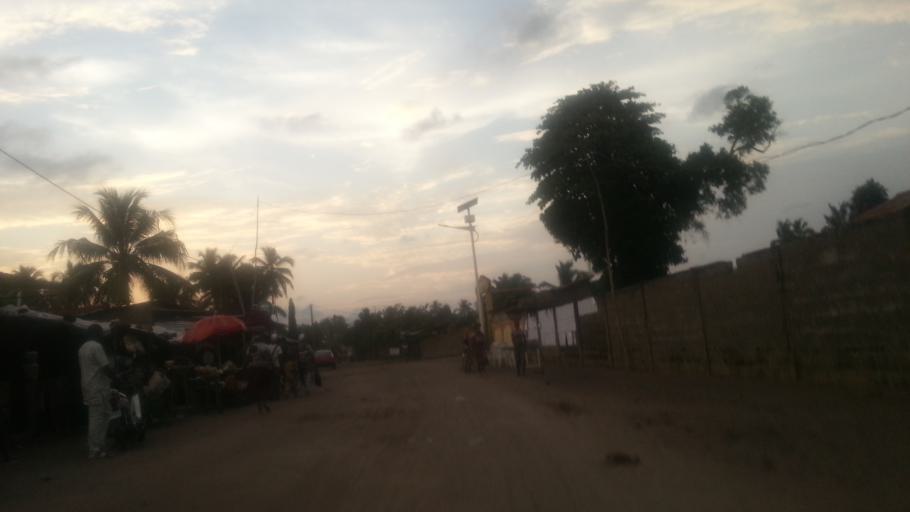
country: BJ
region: Littoral
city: Cotonou
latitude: 6.3877
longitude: 2.5394
